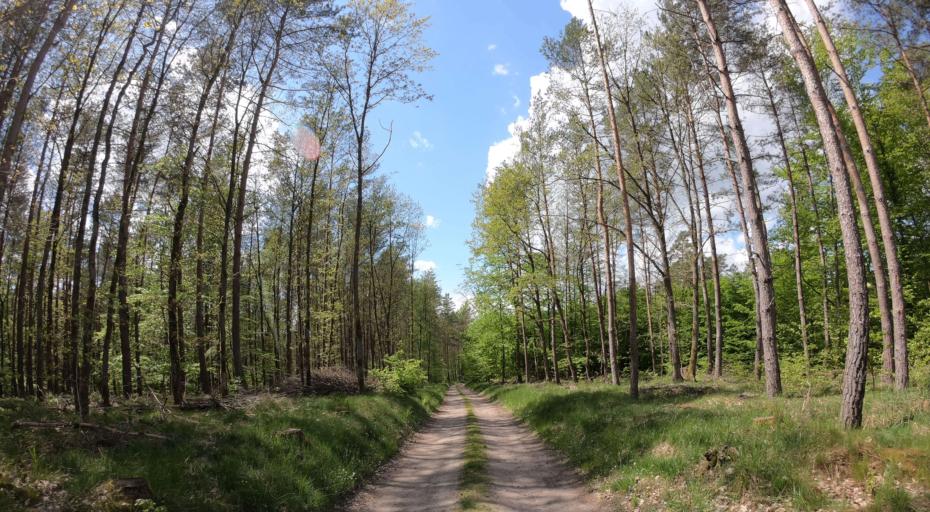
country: PL
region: West Pomeranian Voivodeship
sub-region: Powiat lobeski
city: Lobez
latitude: 53.5972
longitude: 15.6321
